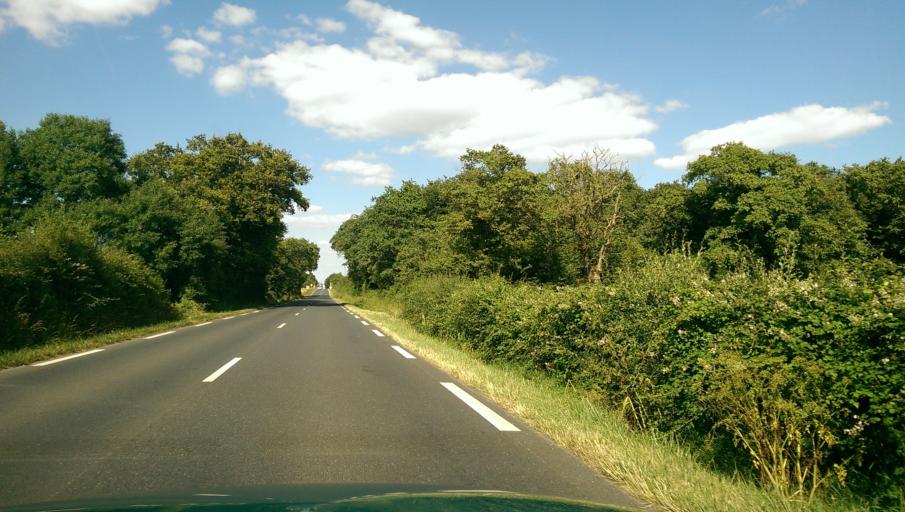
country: FR
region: Pays de la Loire
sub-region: Departement de la Loire-Atlantique
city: Vieillevigne
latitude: 46.9634
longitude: -1.4493
